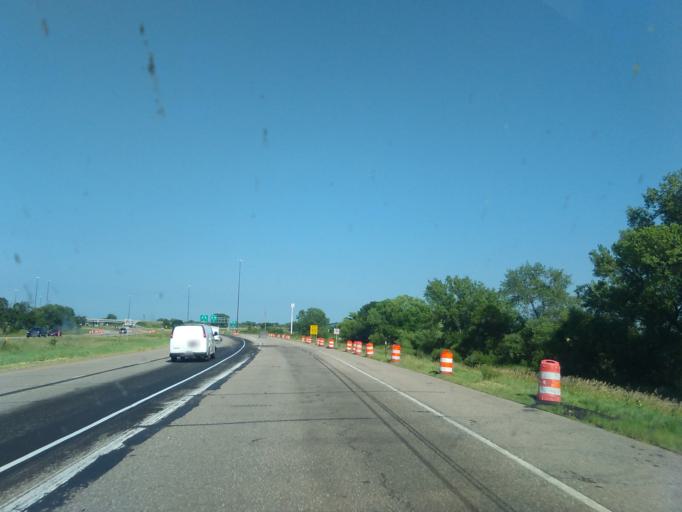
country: US
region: Nebraska
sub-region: Hall County
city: Grand Island
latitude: 40.8194
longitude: -98.3877
